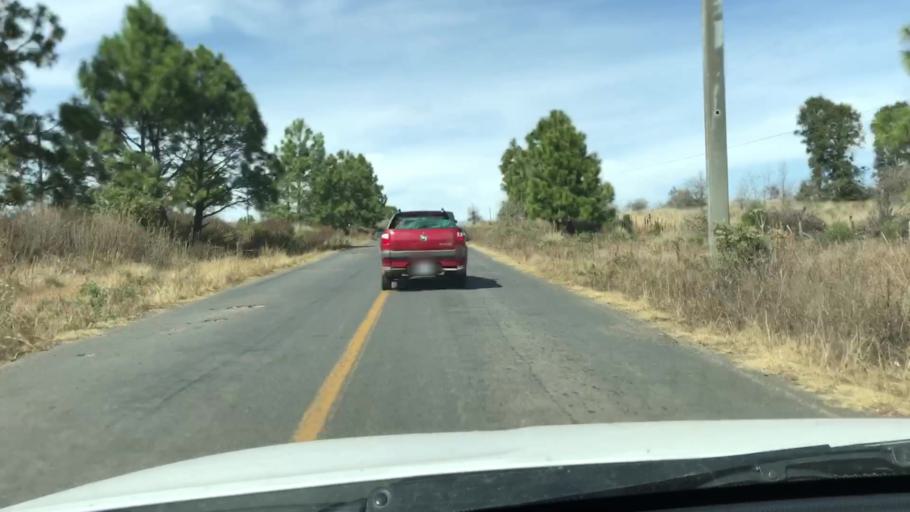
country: MX
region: Jalisco
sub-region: Amacueca
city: Tepec
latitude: 20.0908
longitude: -103.7152
